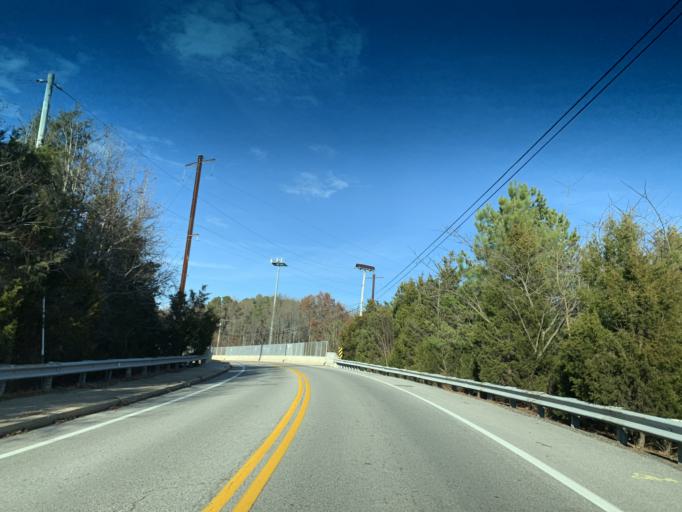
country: US
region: Maryland
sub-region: Cecil County
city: Charlestown
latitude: 39.5813
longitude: -75.9709
